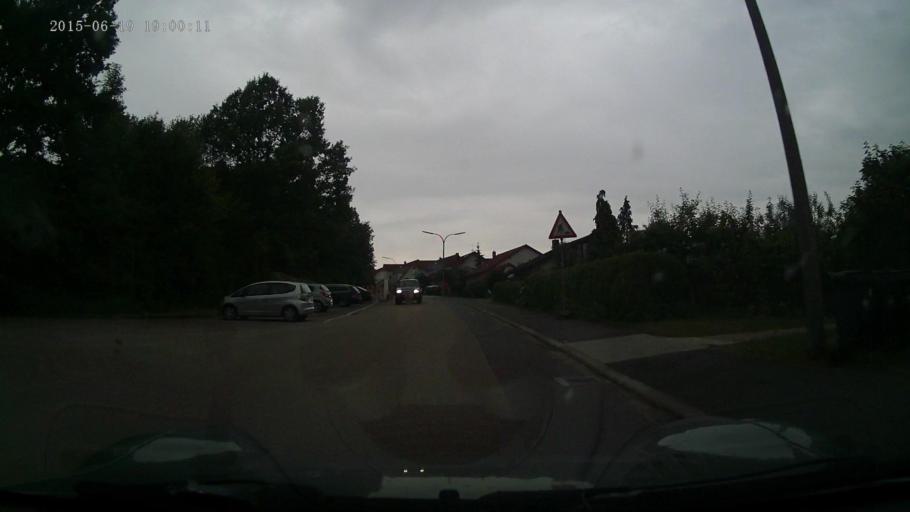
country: DE
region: Baden-Wuerttemberg
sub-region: Karlsruhe Region
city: Osterburken
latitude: 49.4314
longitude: 9.4167
